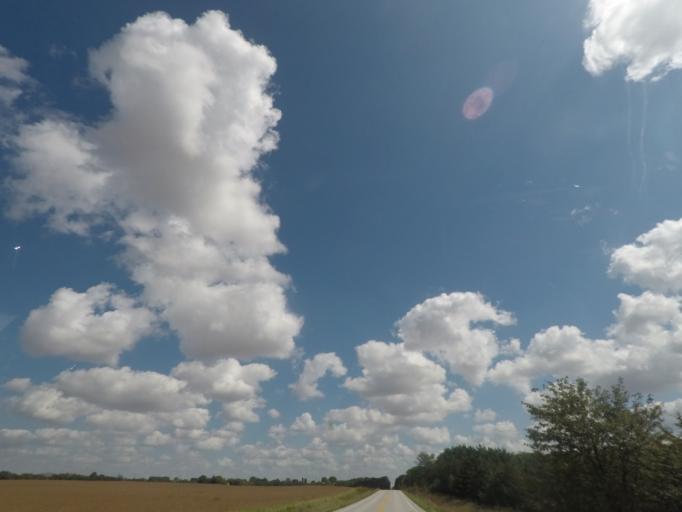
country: US
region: Iowa
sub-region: Story County
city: Nevada
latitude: 42.0778
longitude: -93.3650
